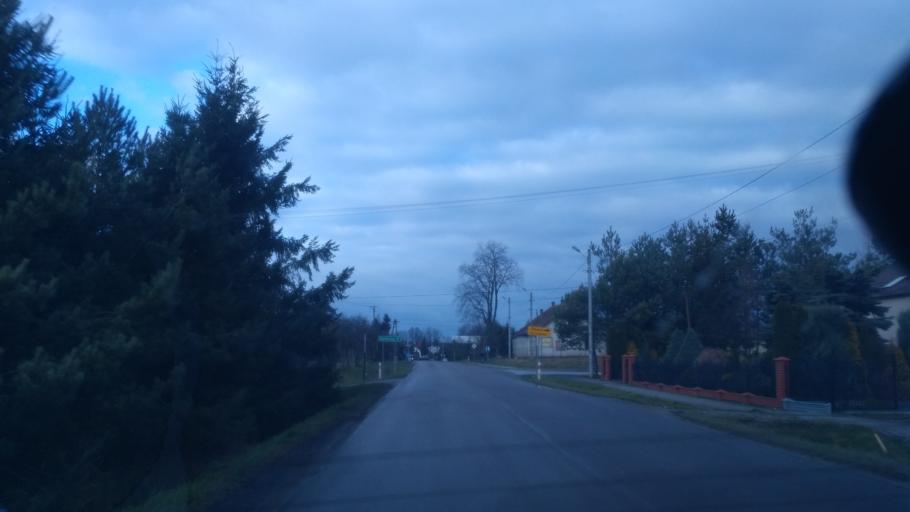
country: PL
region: Subcarpathian Voivodeship
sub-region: Powiat lancucki
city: Czarna
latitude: 50.1087
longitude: 22.1820
